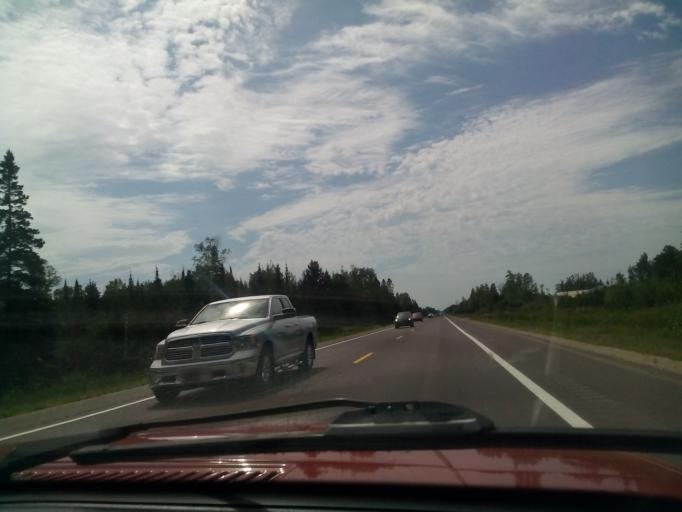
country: US
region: Michigan
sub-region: Schoolcraft County
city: Manistique
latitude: 46.0417
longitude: -85.9723
